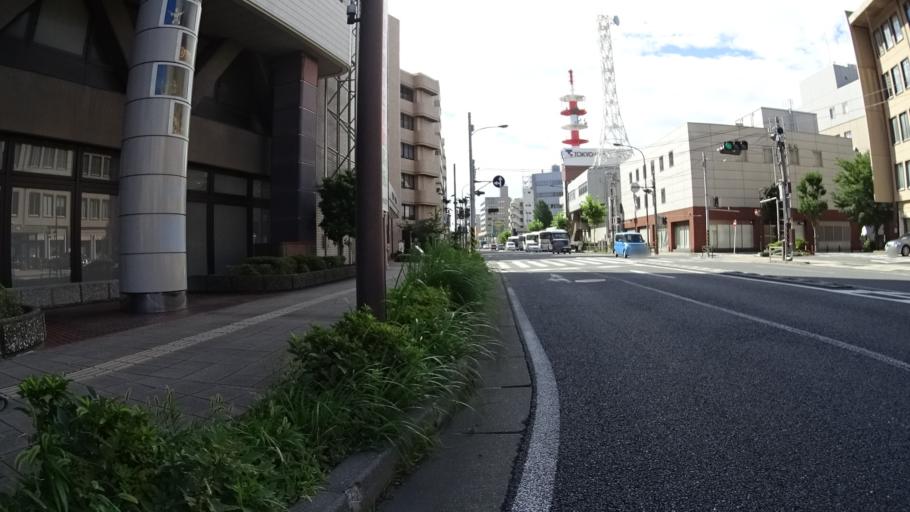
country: JP
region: Kanagawa
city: Yokosuka
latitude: 35.2810
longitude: 139.6720
